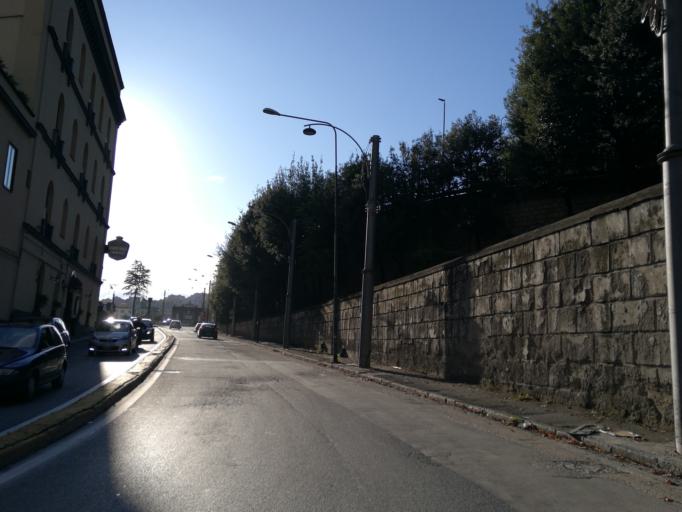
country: IT
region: Campania
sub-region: Provincia di Napoli
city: Napoli
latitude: 40.8661
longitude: 14.2482
